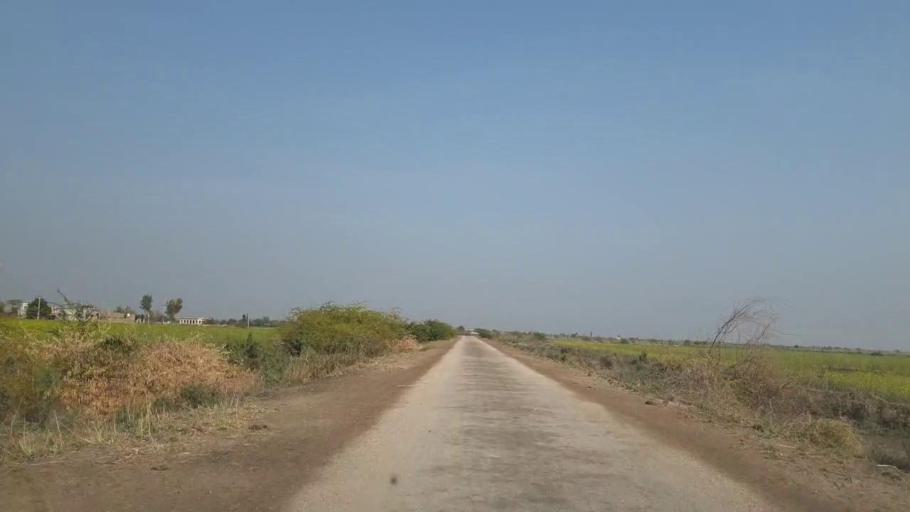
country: PK
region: Sindh
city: Pithoro
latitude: 25.7220
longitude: 69.2176
